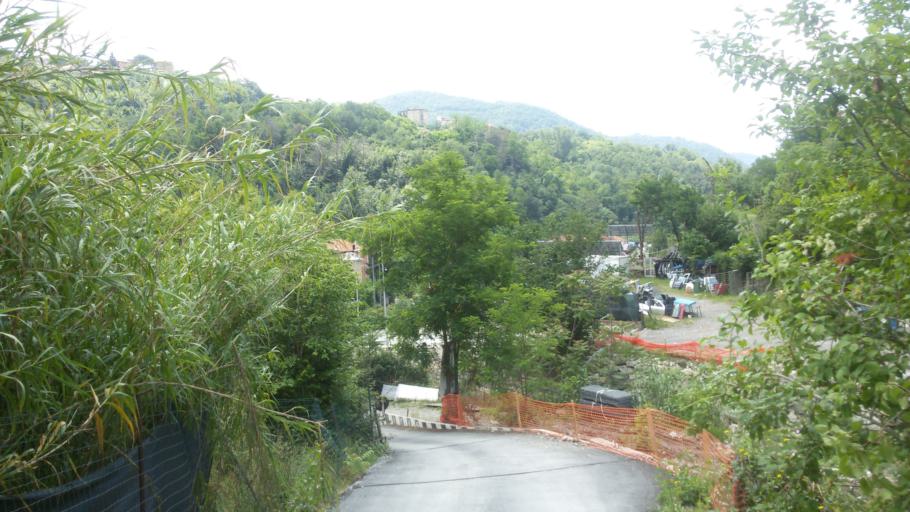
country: IT
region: Liguria
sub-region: Provincia di Genova
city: Piccarello
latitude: 44.4659
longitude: 8.9842
